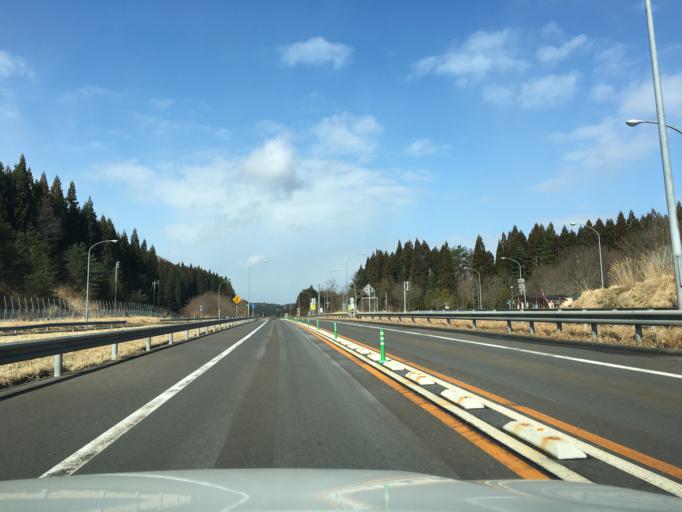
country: JP
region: Akita
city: Akita
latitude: 39.7498
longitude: 140.1515
